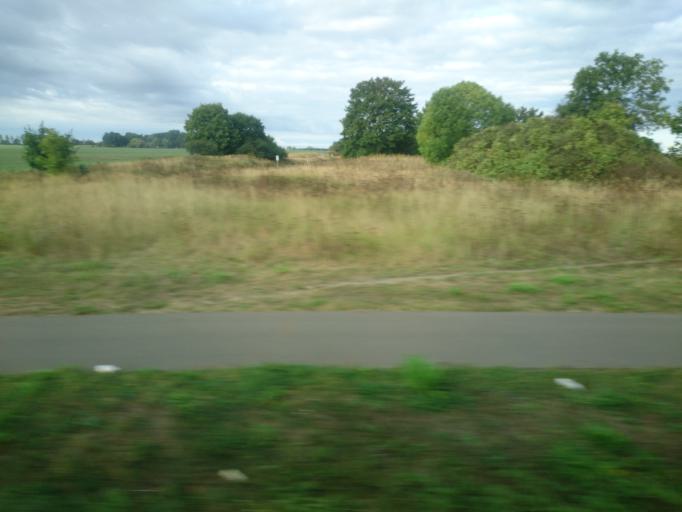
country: DE
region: Mecklenburg-Vorpommern
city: Pasewalk
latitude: 53.5345
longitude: 13.9736
